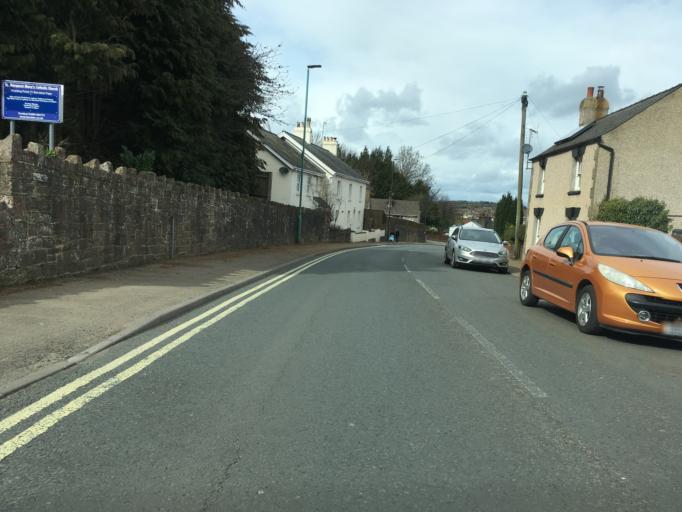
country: GB
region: England
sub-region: Gloucestershire
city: Coleford
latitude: 51.7887
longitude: -2.6167
